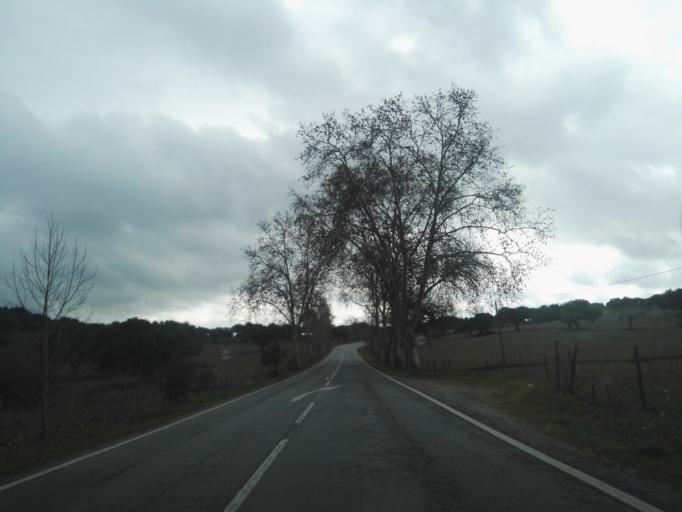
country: PT
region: Portalegre
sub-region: Arronches
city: Arronches
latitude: 39.1061
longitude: -7.2788
